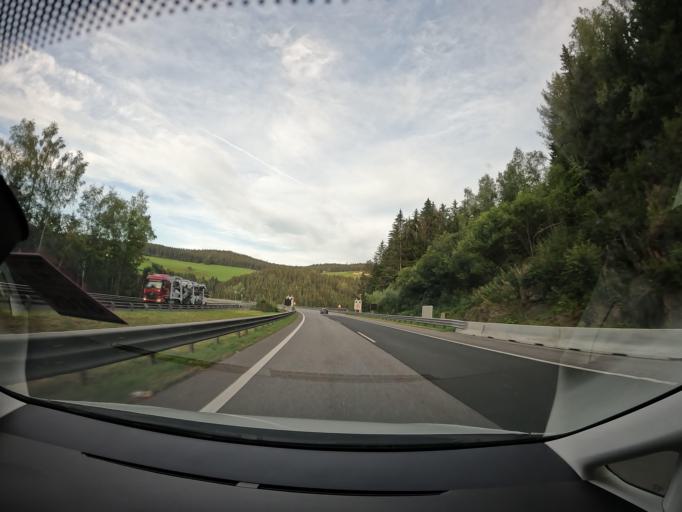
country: AT
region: Styria
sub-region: Politischer Bezirk Voitsberg
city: Pack
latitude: 46.9114
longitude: 14.9897
